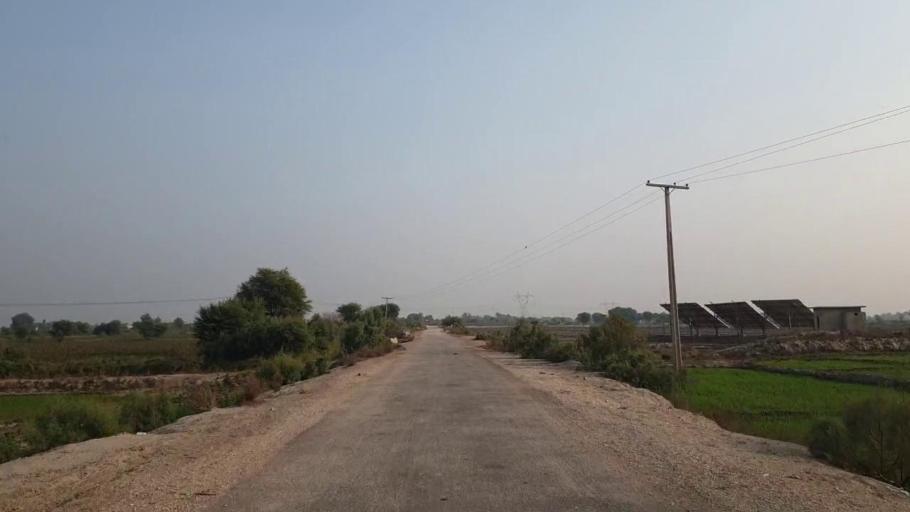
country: PK
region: Sindh
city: Bhan
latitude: 26.4960
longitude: 67.7686
